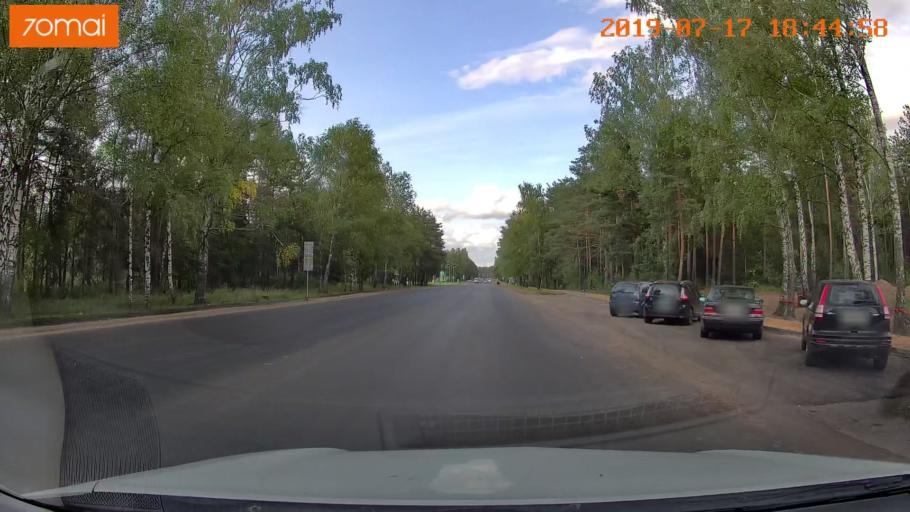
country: BY
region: Mogilev
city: Asipovichy
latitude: 53.3215
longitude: 28.6501
